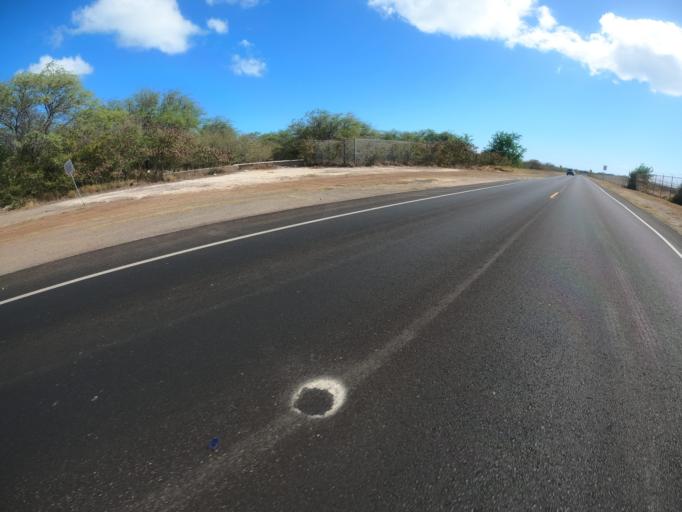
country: US
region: Hawaii
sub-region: Honolulu County
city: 'Ewa Villages
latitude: 21.3191
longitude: -158.0564
